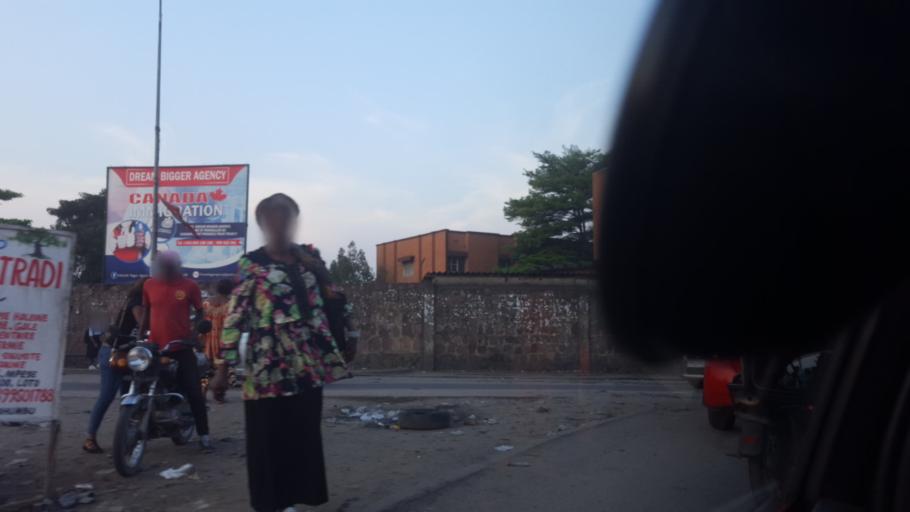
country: CD
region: Kinshasa
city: Kinshasa
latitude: -4.3510
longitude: 15.3251
